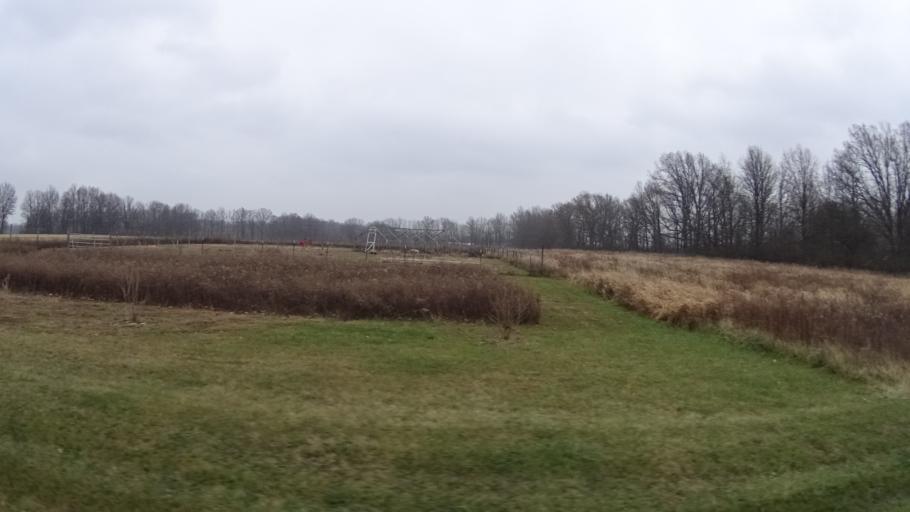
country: US
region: Ohio
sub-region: Lorain County
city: Oberlin
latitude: 41.2854
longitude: -82.1975
